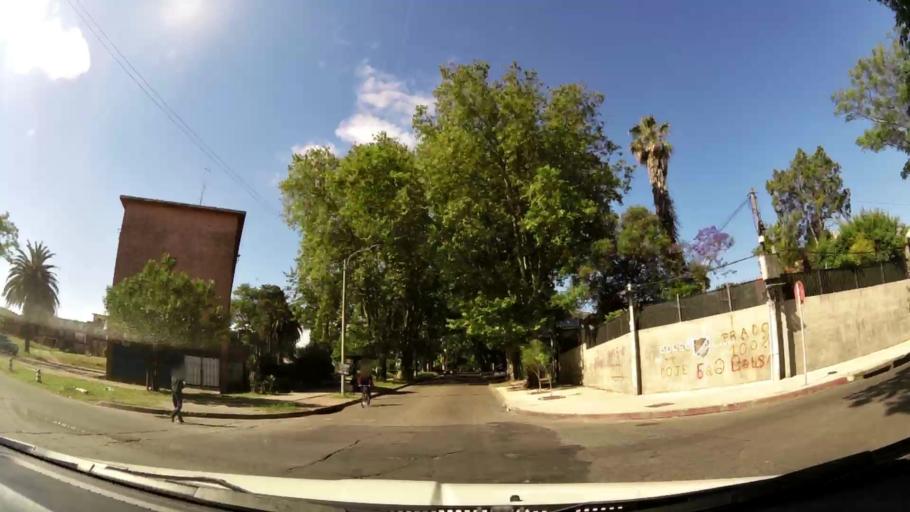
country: UY
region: Montevideo
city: Montevideo
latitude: -34.8447
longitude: -56.2112
